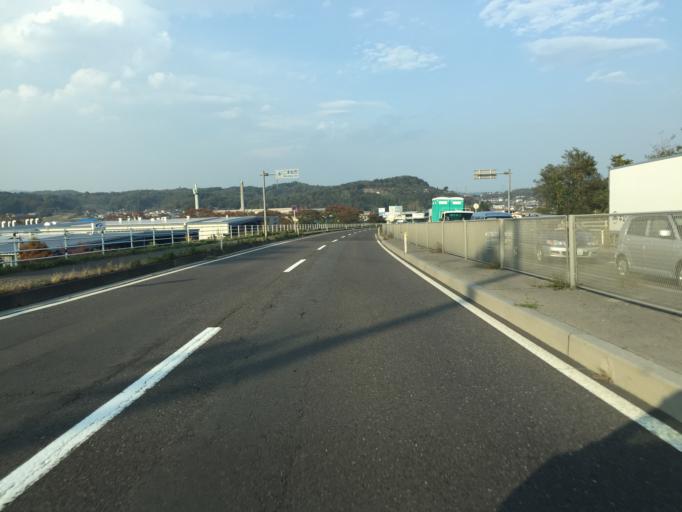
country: JP
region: Fukushima
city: Motomiya
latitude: 37.5548
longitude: 140.4029
